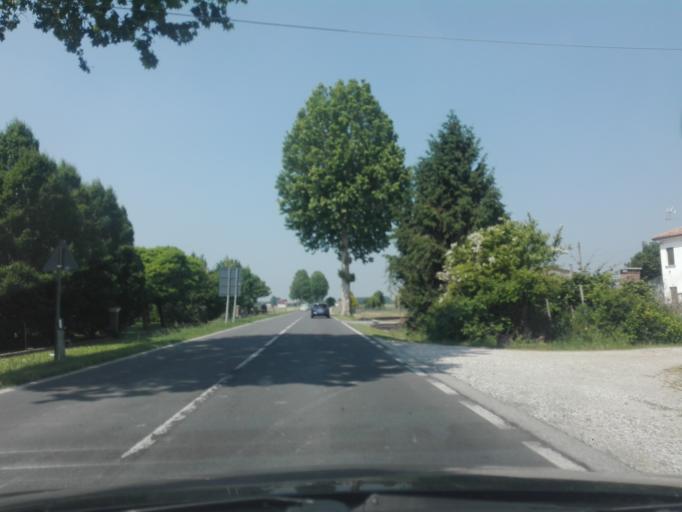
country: IT
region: Veneto
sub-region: Provincia di Rovigo
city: Lama Pezzoli
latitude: 45.0642
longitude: 11.9777
